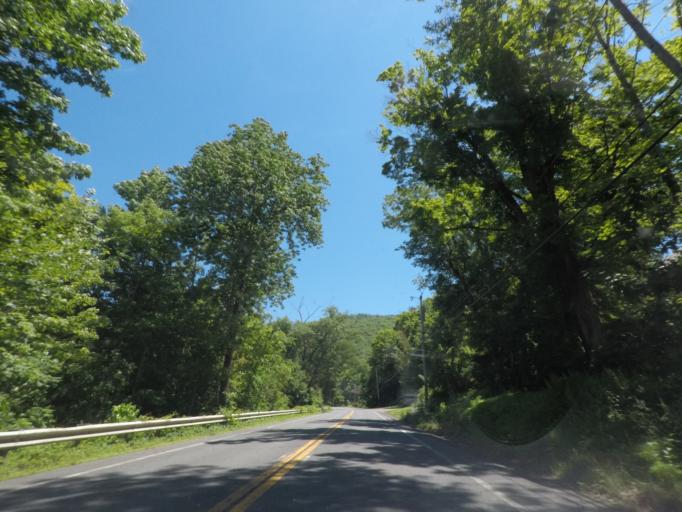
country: US
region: Massachusetts
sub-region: Berkshire County
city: Becket
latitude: 42.2573
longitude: -72.9509
